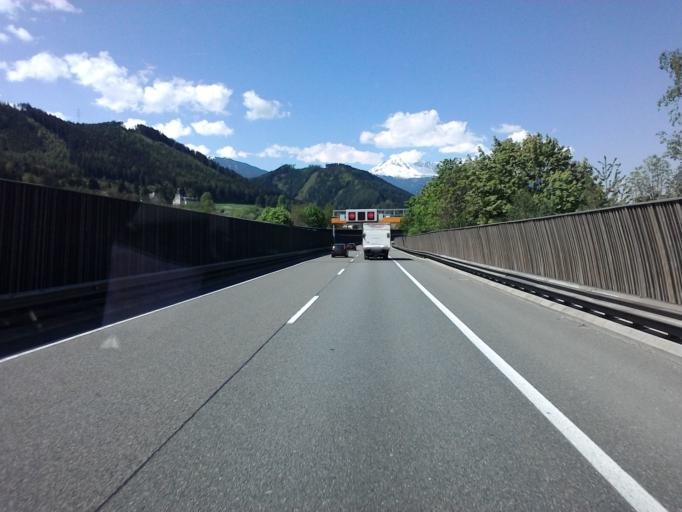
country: AT
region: Tyrol
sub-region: Politischer Bezirk Innsbruck Land
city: Natters
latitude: 47.2536
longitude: 11.3728
